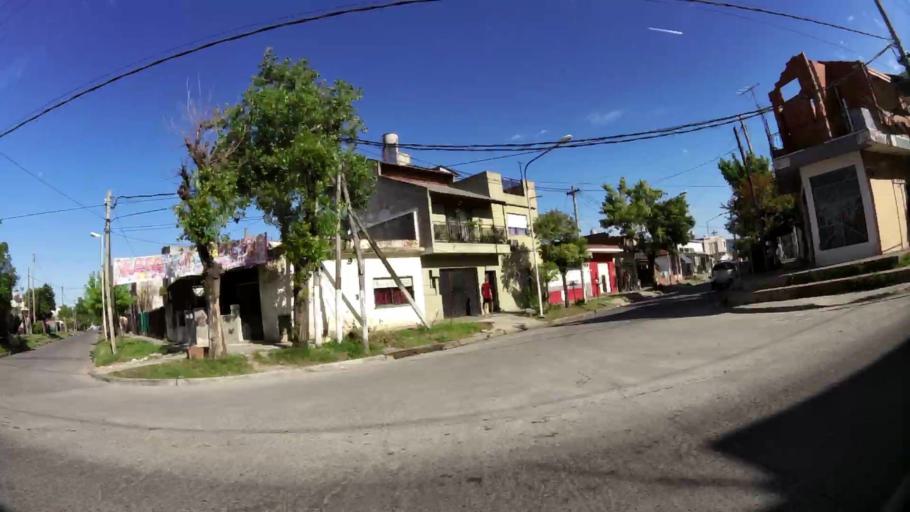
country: AR
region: Buenos Aires
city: Hurlingham
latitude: -34.5576
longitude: -58.6102
